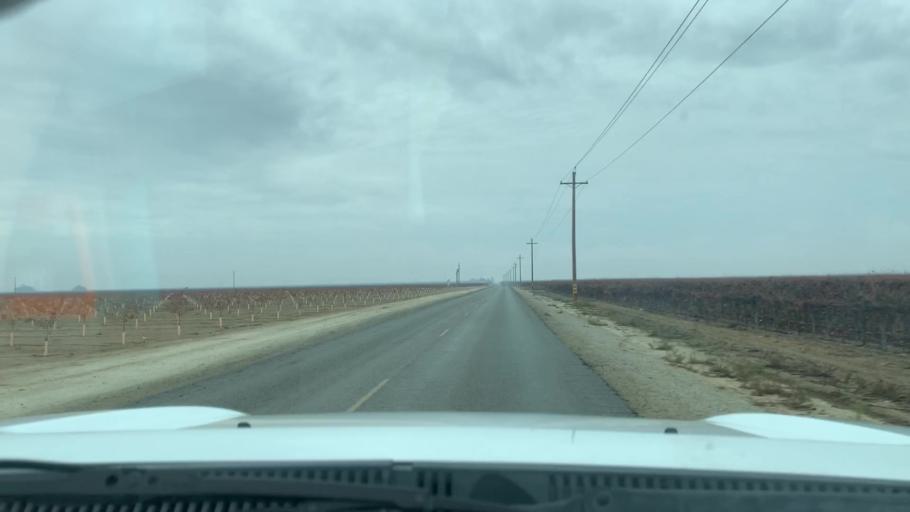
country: US
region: California
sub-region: Kern County
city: Delano
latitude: 35.7611
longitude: -119.3875
